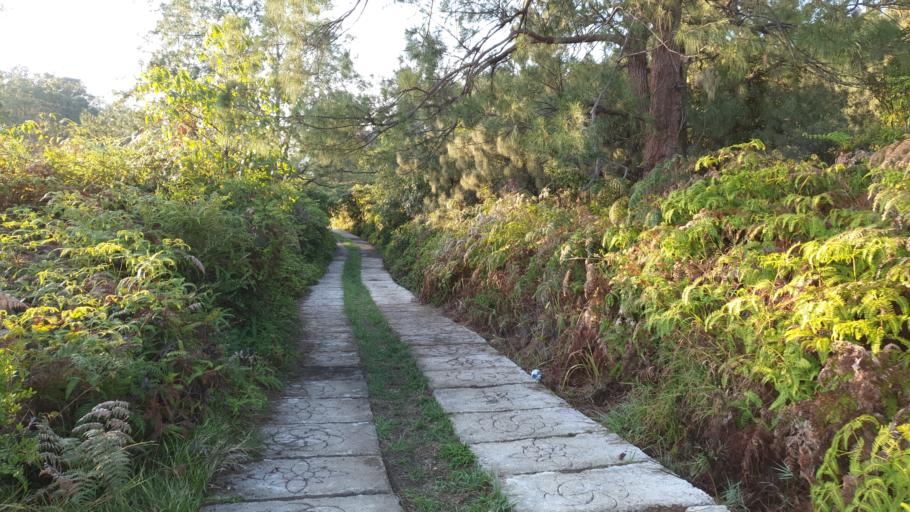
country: ID
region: East Nusa Tenggara
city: Koanara
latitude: -8.7675
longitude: 121.8126
